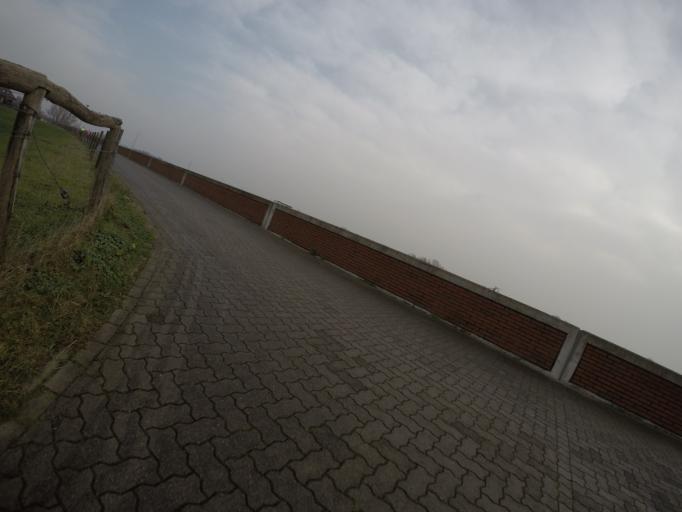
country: DE
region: North Rhine-Westphalia
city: Rees
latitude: 51.7324
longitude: 6.4137
